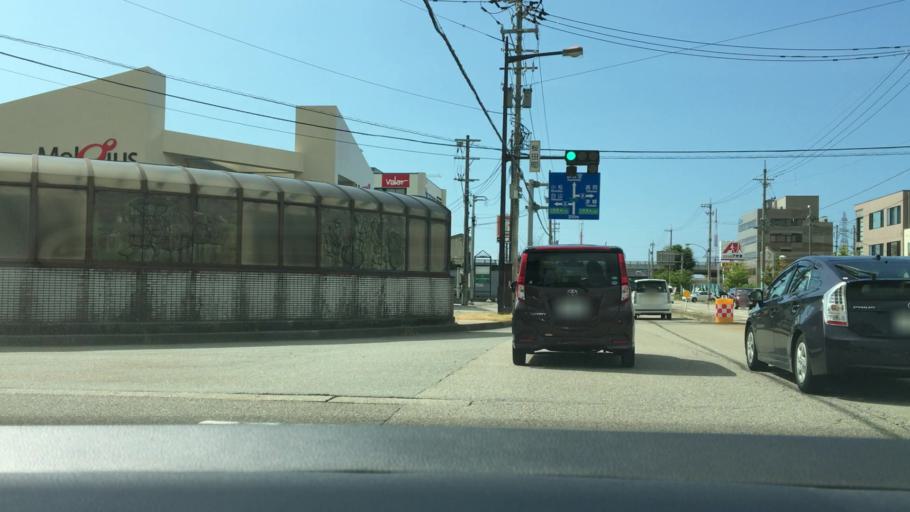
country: JP
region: Ishikawa
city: Kanazawa-shi
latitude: 36.5774
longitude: 136.6191
